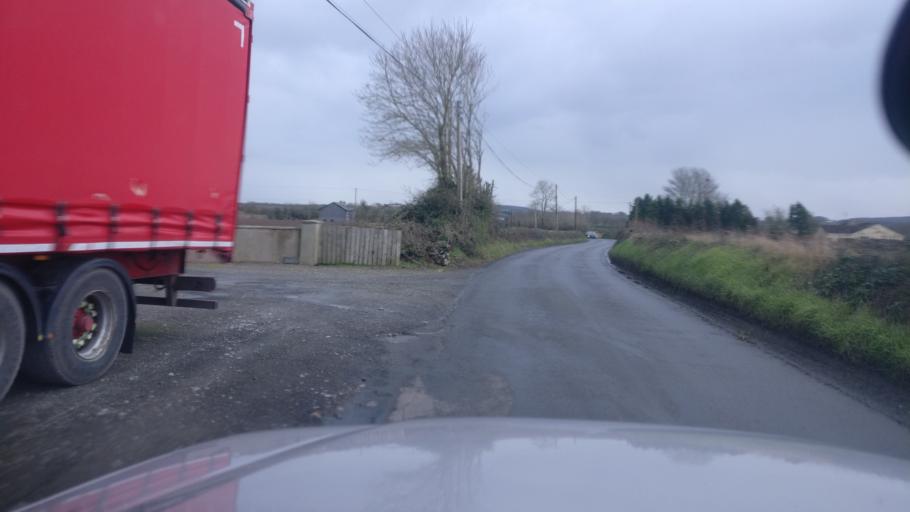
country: IE
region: Munster
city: Nenagh Bridge
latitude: 52.9870
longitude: -8.1126
